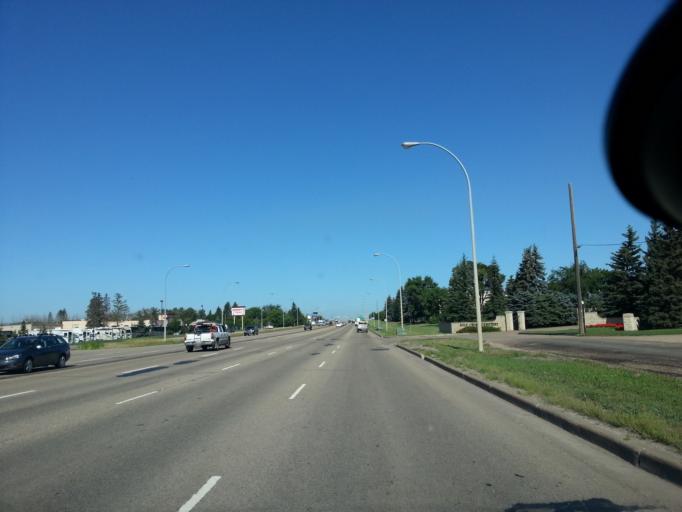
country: CA
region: Alberta
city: St. Albert
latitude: 53.6066
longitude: -113.5822
